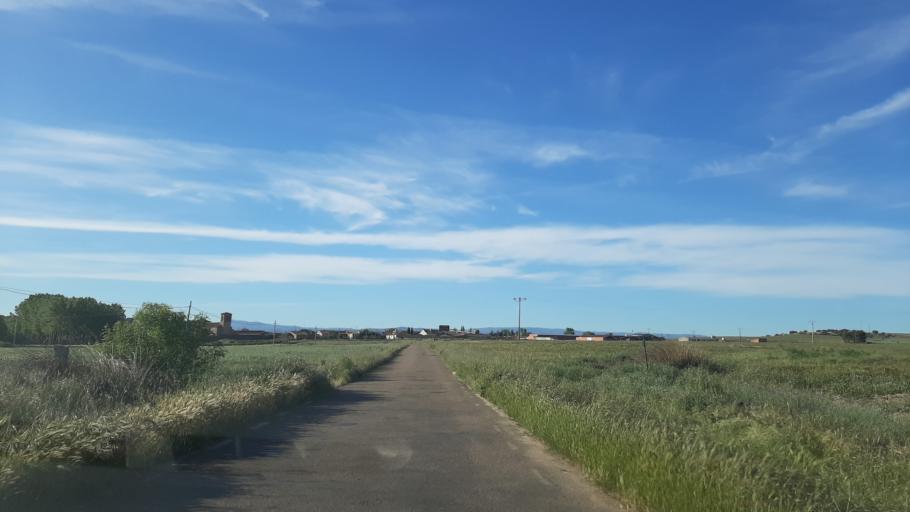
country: ES
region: Castille and Leon
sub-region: Provincia de Salamanca
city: Gajates
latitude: 40.7866
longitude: -5.3688
